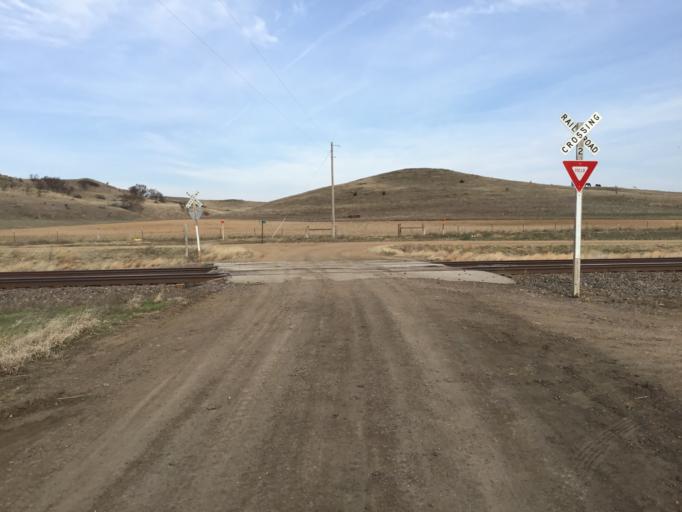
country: US
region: Kansas
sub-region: Ellsworth County
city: Ellsworth
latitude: 38.7438
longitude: -97.9343
